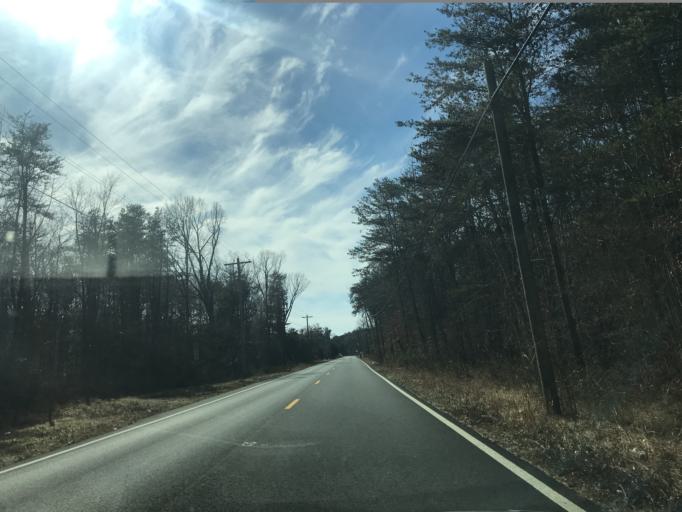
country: US
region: Maryland
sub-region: Charles County
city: Indian Head
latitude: 38.5276
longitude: -77.1430
